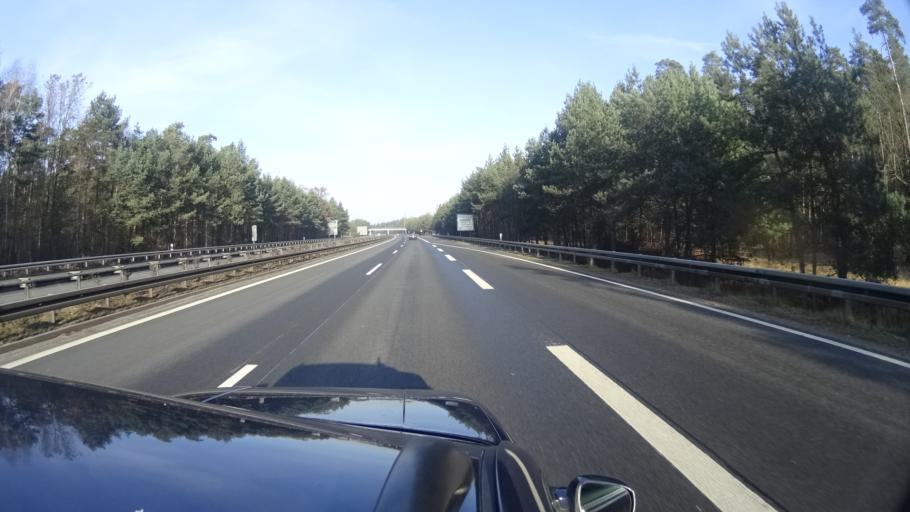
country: DE
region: Brandenburg
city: Hohen Neuendorf
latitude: 52.6571
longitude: 13.2440
